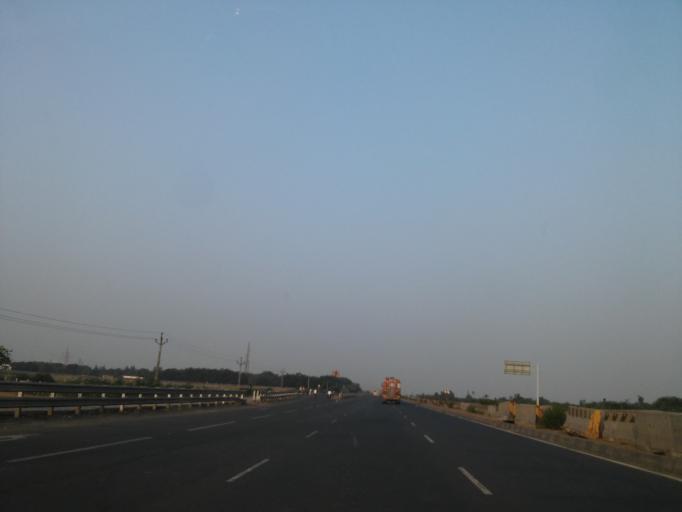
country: IN
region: Gujarat
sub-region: Kachchh
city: Bhachau
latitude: 23.3102
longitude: 70.4829
